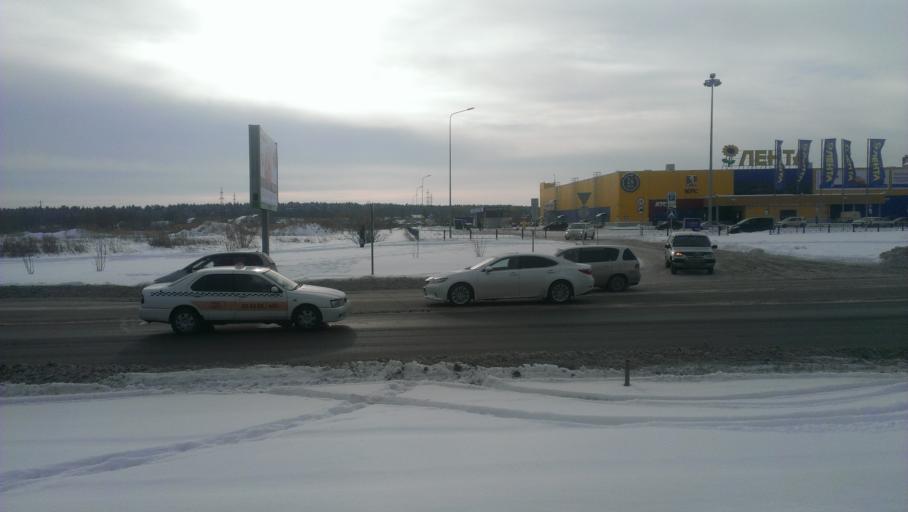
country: RU
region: Altai Krai
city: Novosilikatnyy
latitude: 53.3280
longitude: 83.6870
